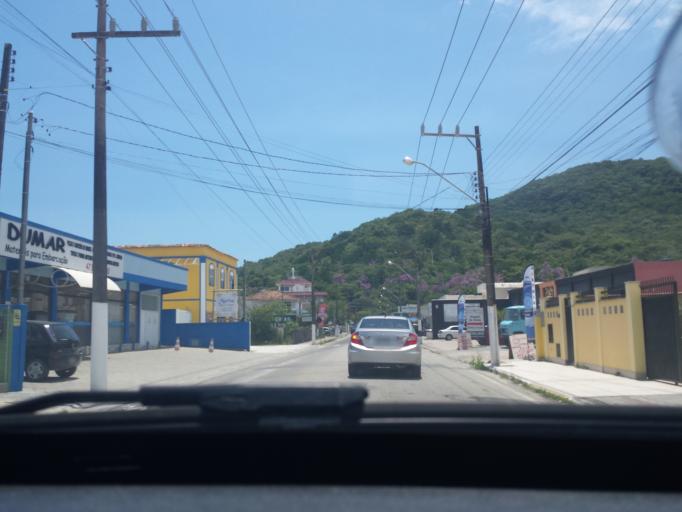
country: BR
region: Santa Catarina
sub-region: Porto Belo
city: Porto Belo
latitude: -27.1531
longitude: -48.5393
